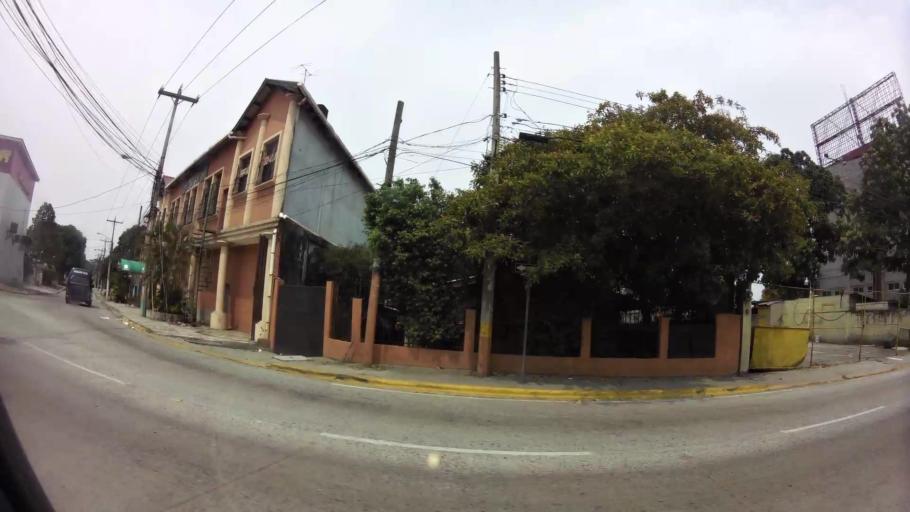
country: HN
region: Cortes
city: San Pedro Sula
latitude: 15.4914
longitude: -88.0349
